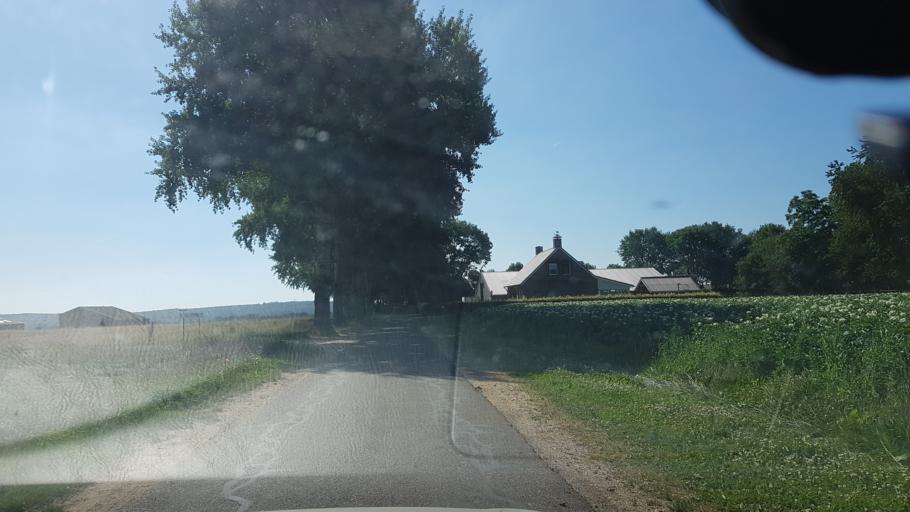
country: NL
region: Gelderland
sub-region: Gemeente Groesbeek
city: Bredeweg
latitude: 51.7575
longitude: 5.9227
